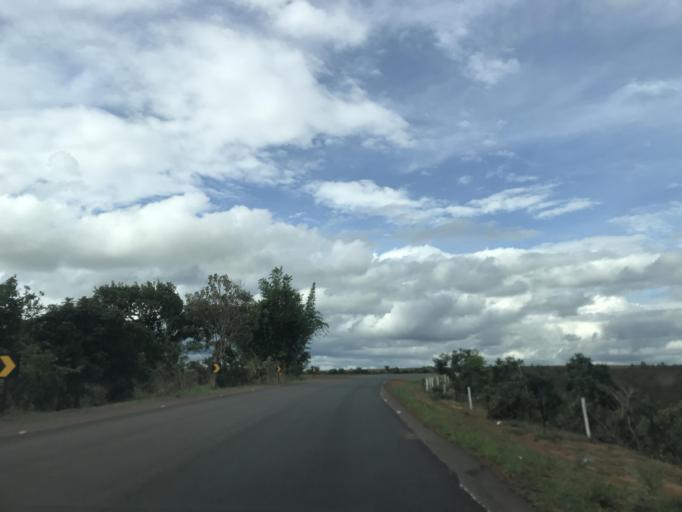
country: BR
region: Goias
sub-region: Vianopolis
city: Vianopolis
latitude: -16.9818
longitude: -48.6679
